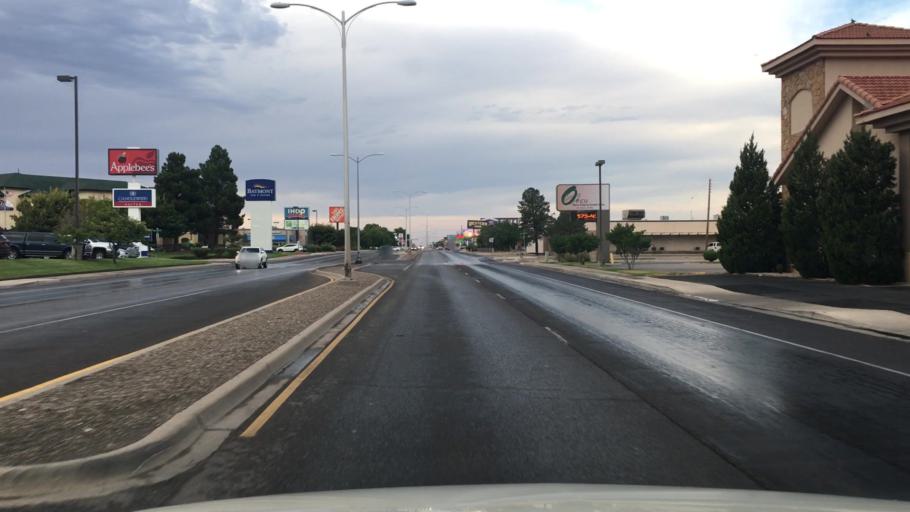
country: US
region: New Mexico
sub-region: Chaves County
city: Roswell
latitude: 33.4188
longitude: -104.5230
